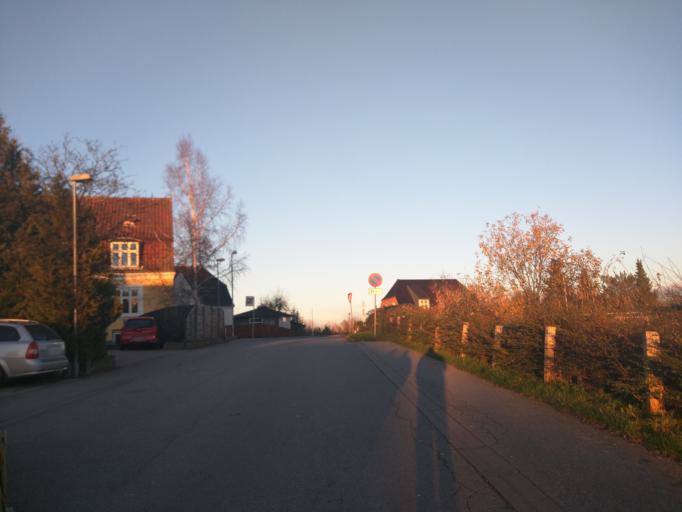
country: DK
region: Central Jutland
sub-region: Skanderborg Kommune
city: Horning
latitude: 56.0828
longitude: 10.0382
